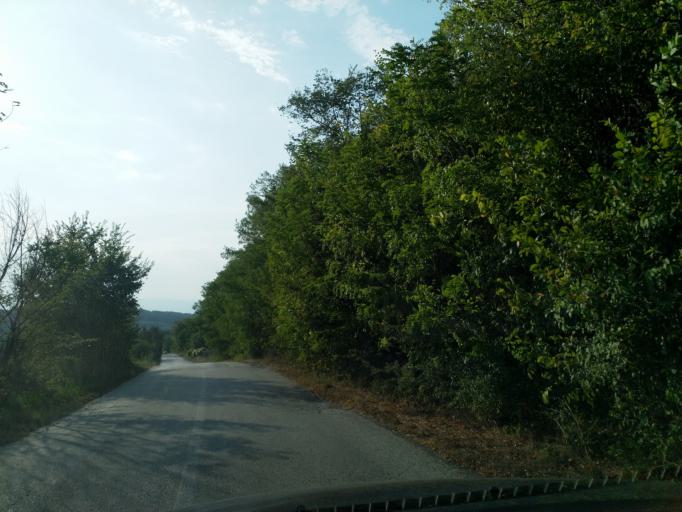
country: RS
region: Central Serbia
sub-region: Pomoravski Okrug
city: Paracin
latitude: 43.8409
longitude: 21.5373
